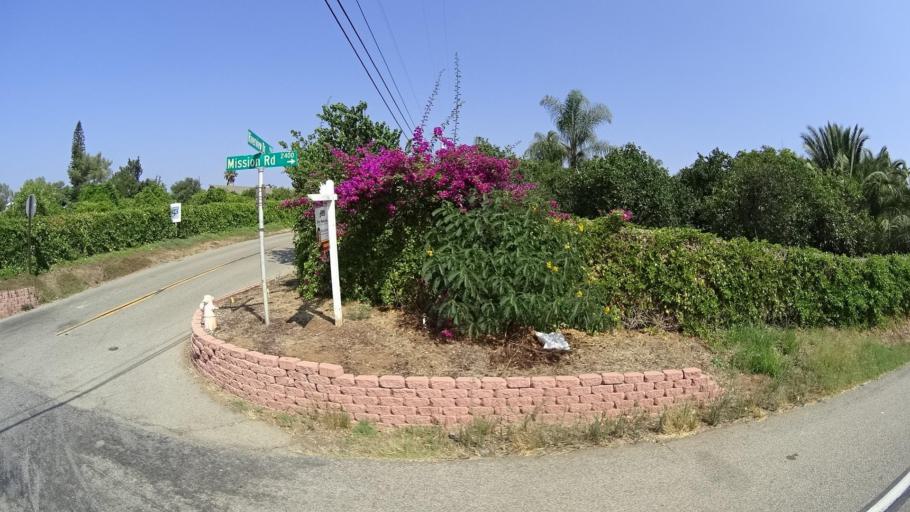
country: US
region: California
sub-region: San Diego County
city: Fallbrook
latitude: 33.3917
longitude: -117.2121
